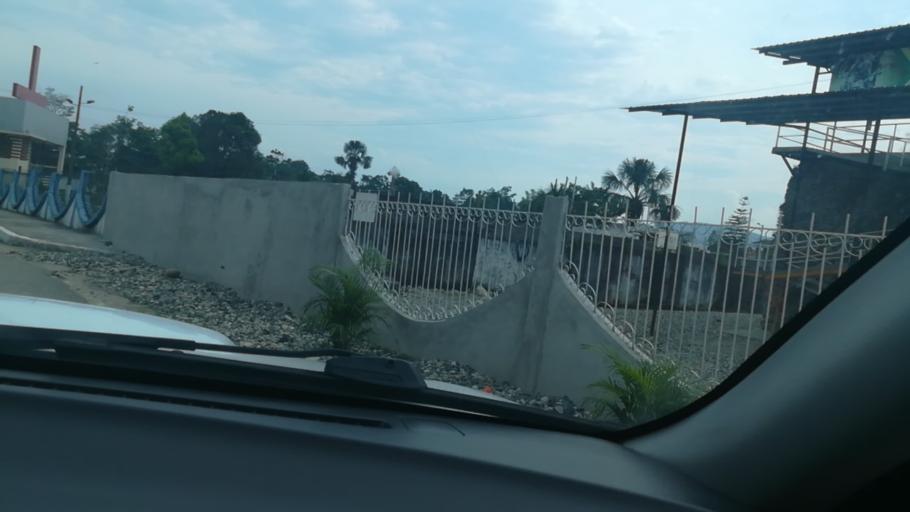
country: EC
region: Napo
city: Tena
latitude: -0.9733
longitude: -77.8155
